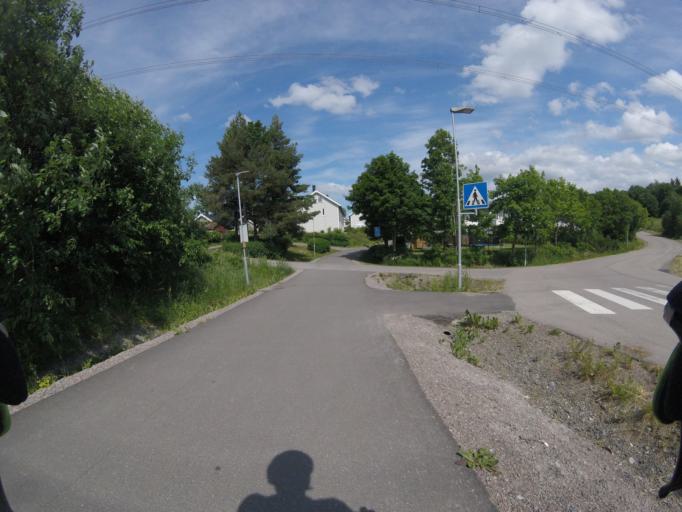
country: NO
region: Akershus
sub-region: Skedsmo
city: Lillestrom
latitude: 59.9894
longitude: 11.0361
